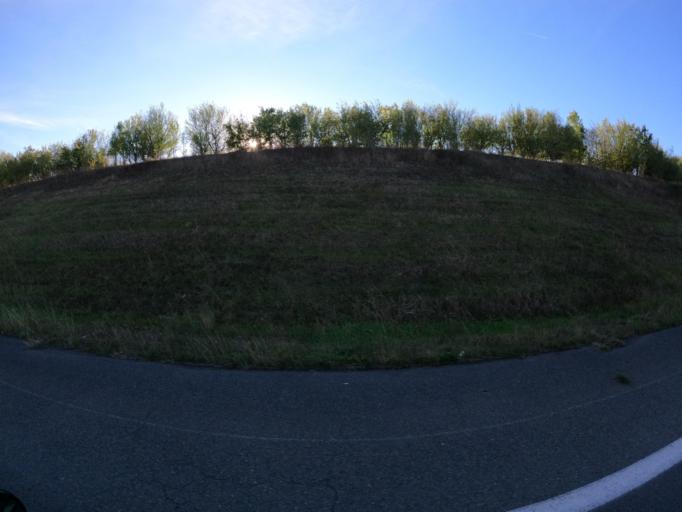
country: FR
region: Pays de la Loire
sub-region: Departement de Maine-et-Loire
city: Nuaille
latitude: 47.0990
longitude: -0.8253
